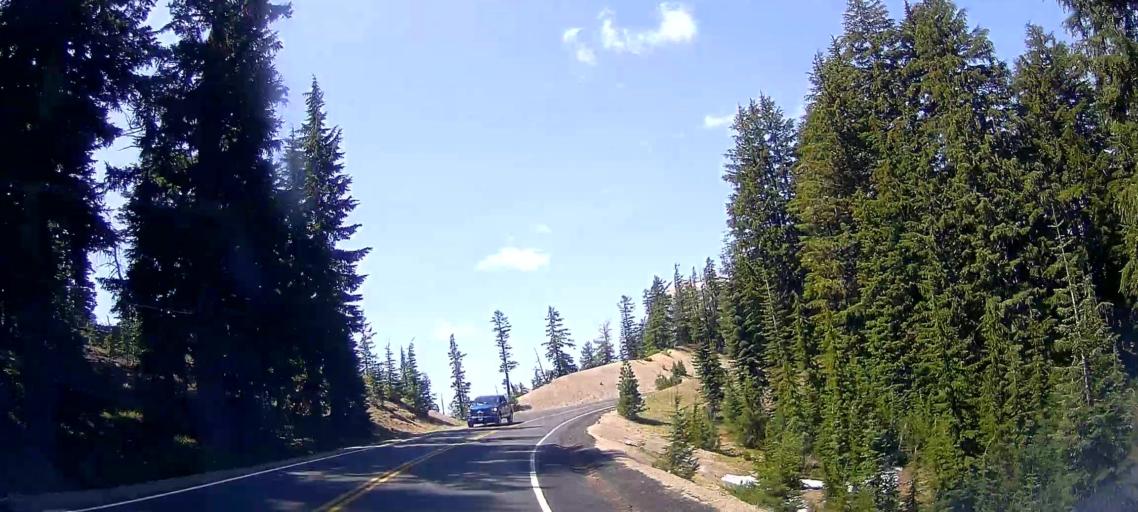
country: US
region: Oregon
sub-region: Jackson County
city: Shady Cove
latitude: 42.9805
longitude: -122.1117
